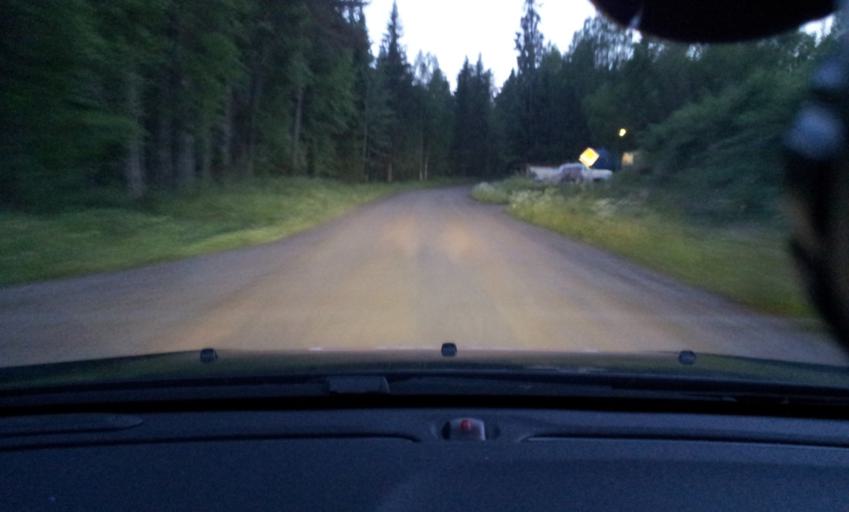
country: SE
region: Jaemtland
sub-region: Braecke Kommun
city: Braecke
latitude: 62.7199
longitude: 15.5784
